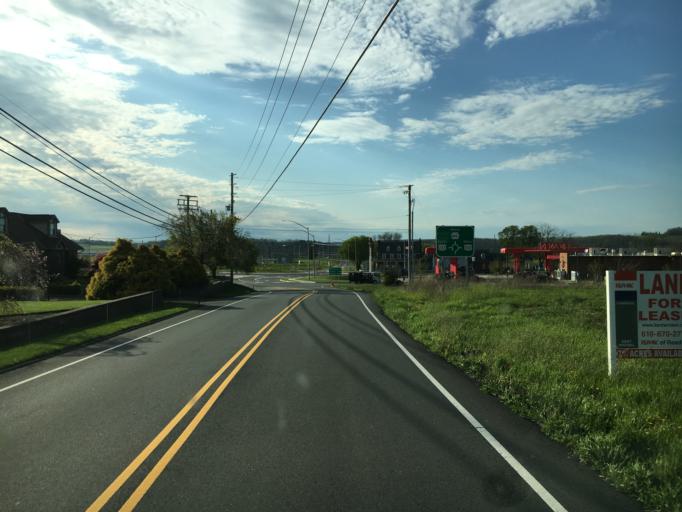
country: US
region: Pennsylvania
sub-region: Berks County
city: Fleetwood
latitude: 40.4843
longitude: -75.8374
